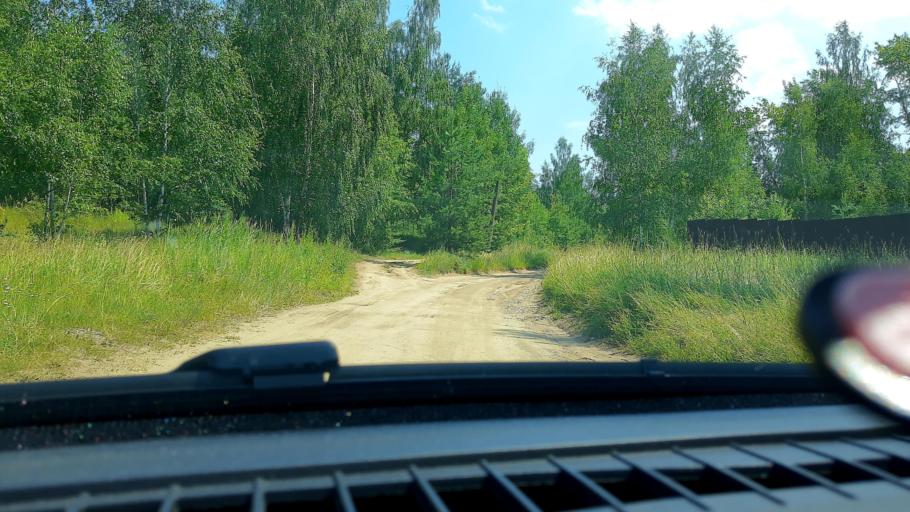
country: RU
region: Nizjnij Novgorod
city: Zavolzh'ye
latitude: 56.6886
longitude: 43.4261
